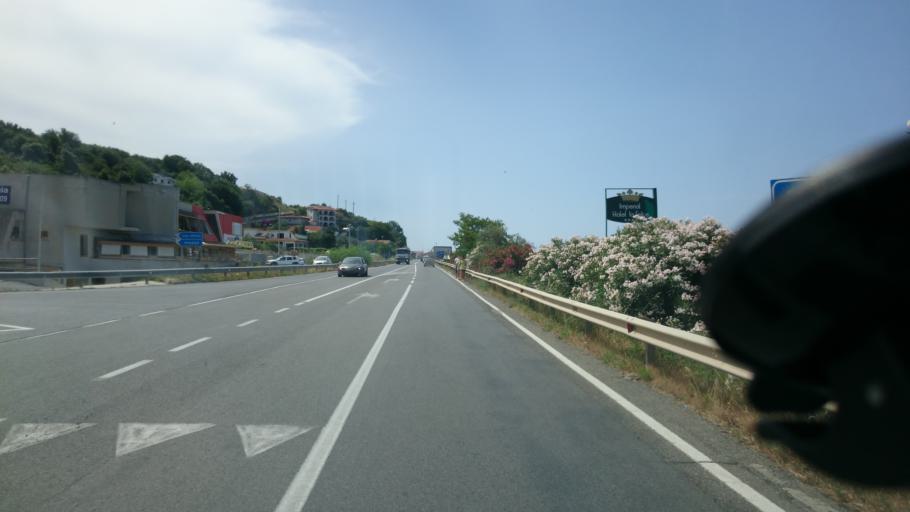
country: IT
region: Calabria
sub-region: Provincia di Cosenza
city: Diamante
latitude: 39.6849
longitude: 15.8196
